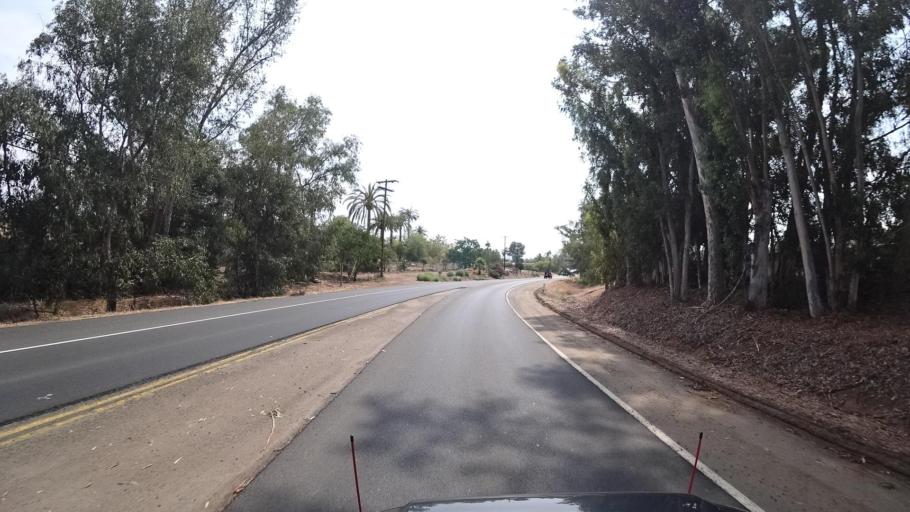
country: US
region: California
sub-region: San Diego County
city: Escondido
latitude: 33.1146
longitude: -117.0577
